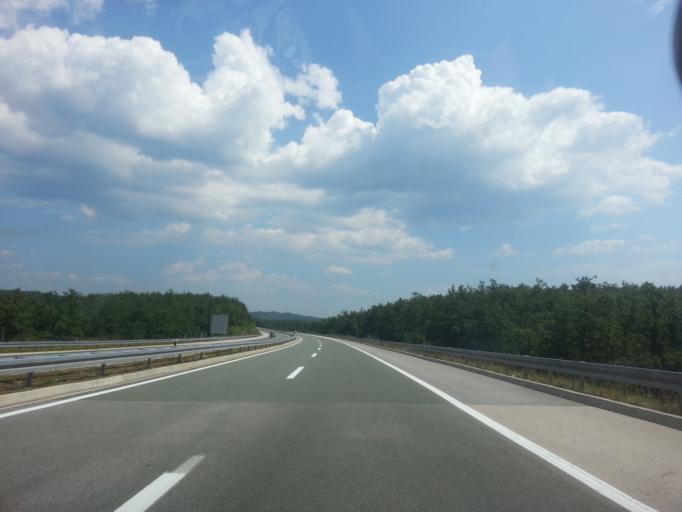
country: HR
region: Primorsko-Goranska
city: Matulji
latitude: 45.4369
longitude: 14.2785
